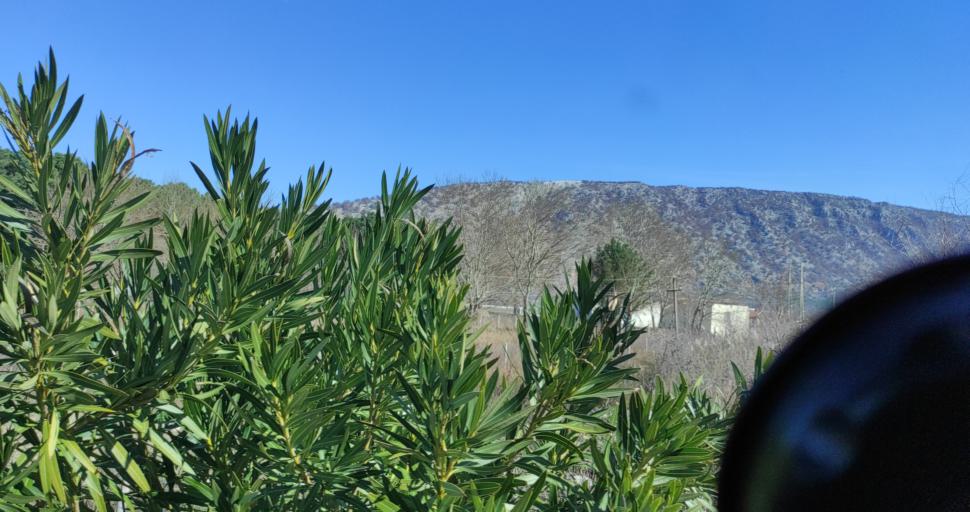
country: AL
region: Shkoder
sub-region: Rrethi i Shkodres
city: Velipoje
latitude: 41.8618
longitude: 19.4460
